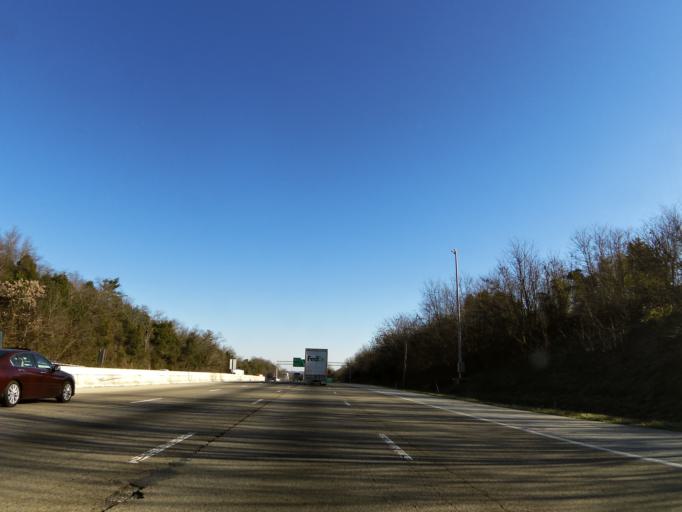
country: US
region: Tennessee
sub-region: Jefferson County
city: Dandridge
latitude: 36.0574
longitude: -83.4044
